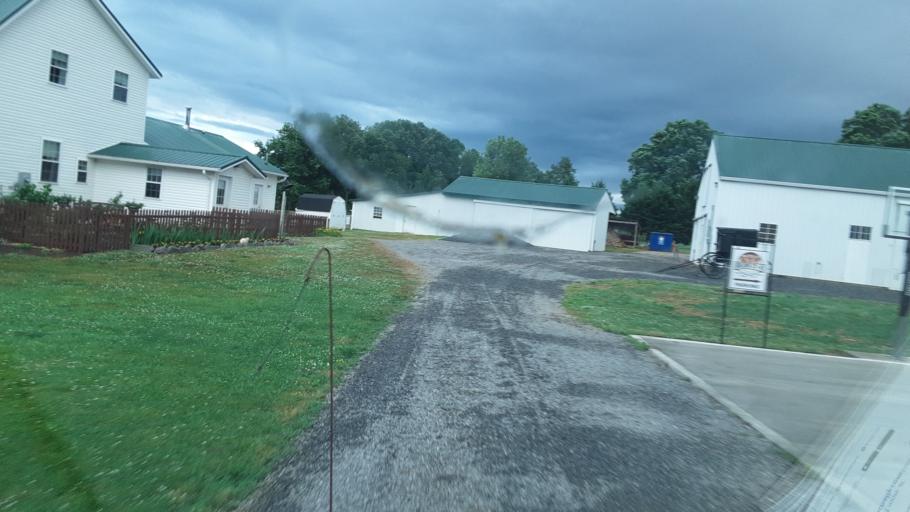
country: US
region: North Carolina
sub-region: Yadkin County
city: Jonesville
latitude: 36.0794
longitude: -80.8750
